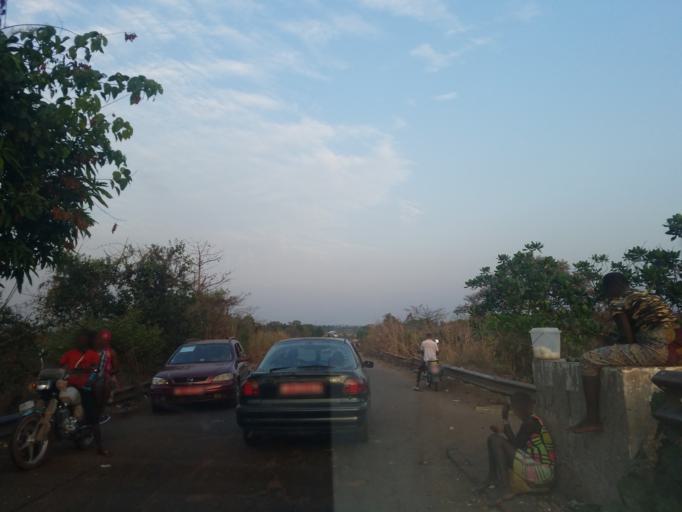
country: GN
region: Boke
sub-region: Fria
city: Fria
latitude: 10.0879
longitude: -13.6722
